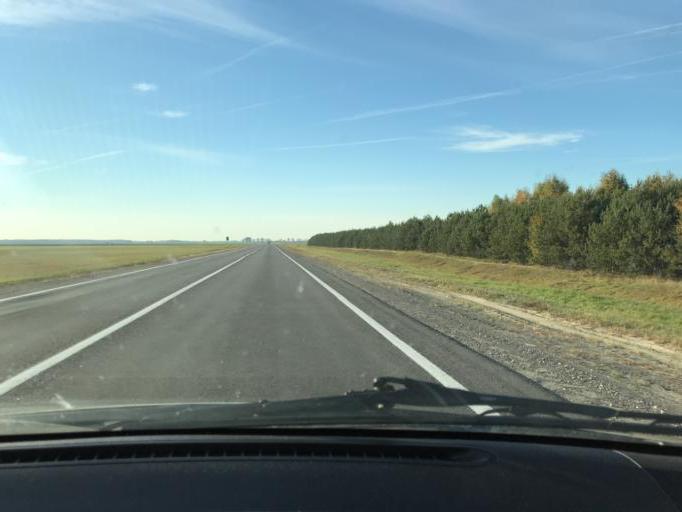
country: BY
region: Brest
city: Antopal'
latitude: 52.2213
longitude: 24.8398
